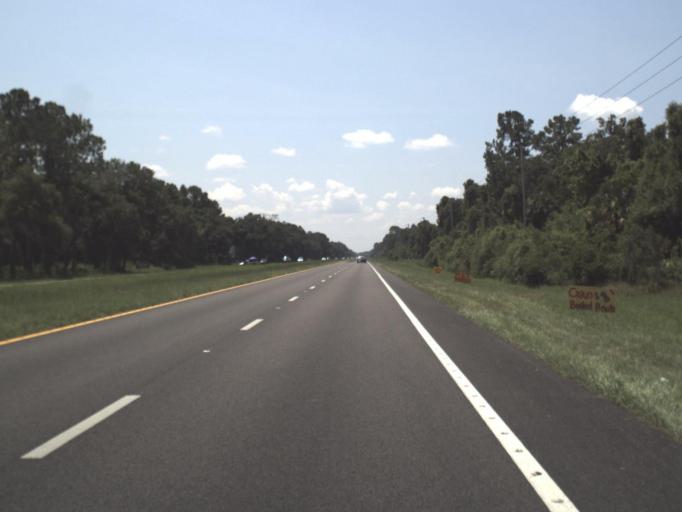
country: US
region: Florida
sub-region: Citrus County
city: Crystal River
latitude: 28.9402
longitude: -82.6208
